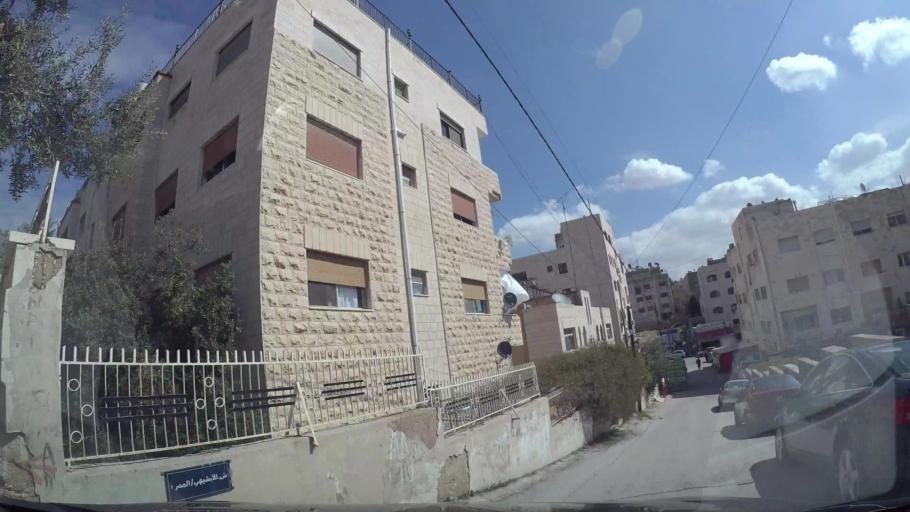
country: JO
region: Amman
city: Al Jubayhah
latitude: 31.9899
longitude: 35.9030
